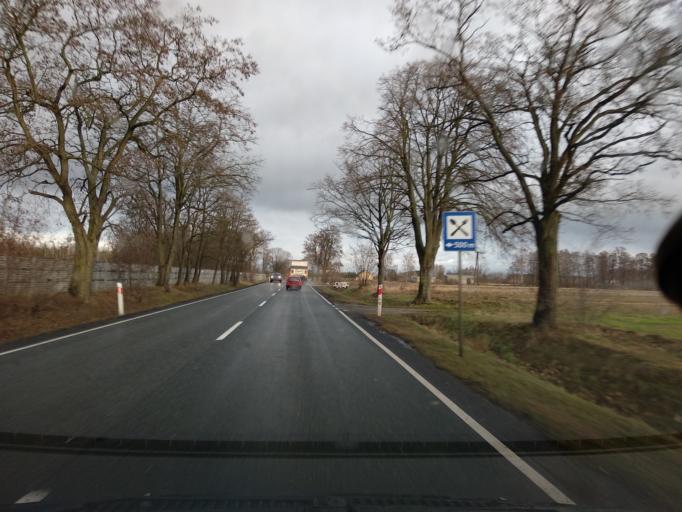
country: PL
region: Greater Poland Voivodeship
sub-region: Powiat koninski
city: Stare Miasto
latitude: 52.1330
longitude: 18.1834
